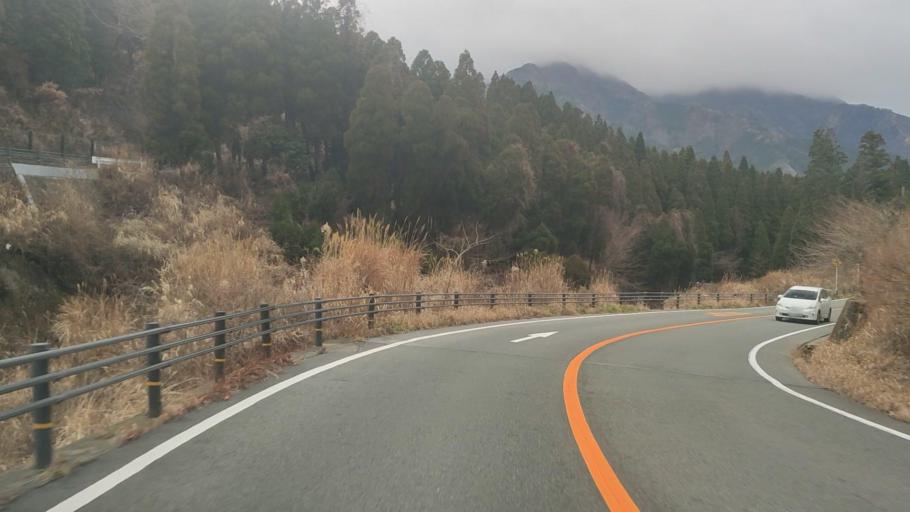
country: JP
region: Kumamoto
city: Aso
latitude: 32.9105
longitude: 131.1428
